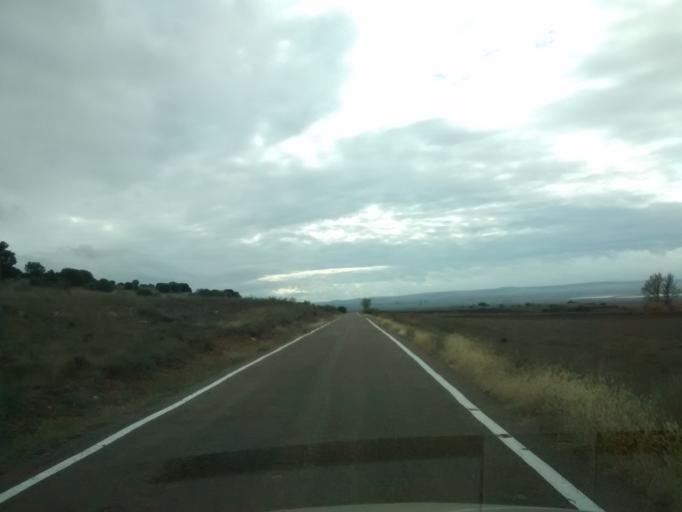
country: ES
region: Aragon
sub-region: Provincia de Teruel
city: Tornos
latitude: 40.9814
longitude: -1.4665
